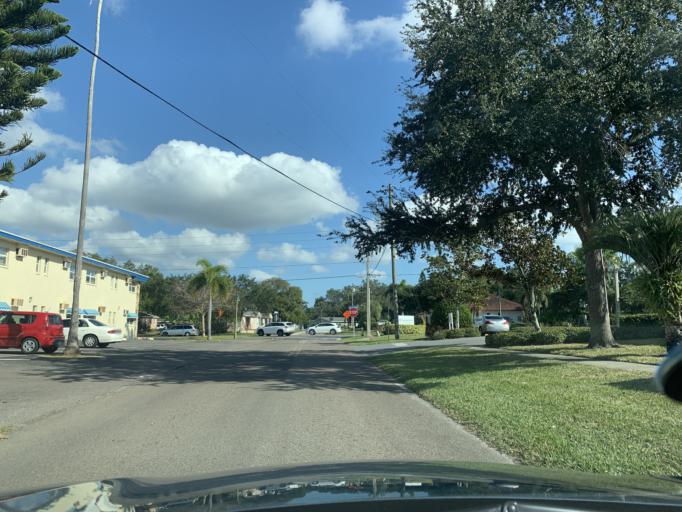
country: US
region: Florida
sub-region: Pinellas County
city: Belleair
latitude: 27.9259
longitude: -82.7969
